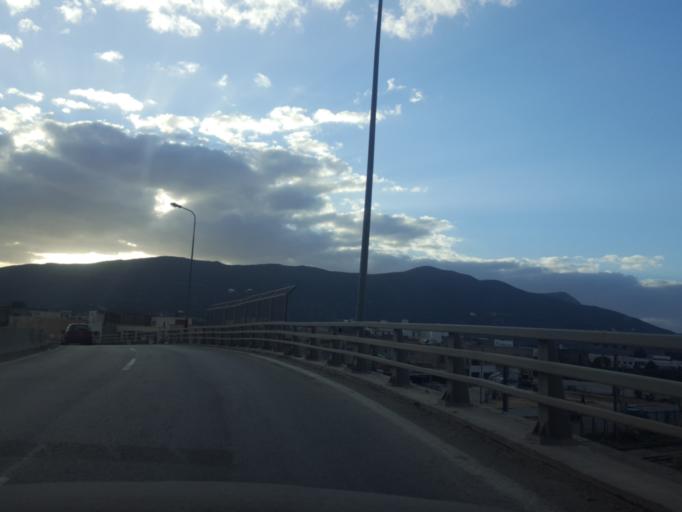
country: TN
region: Tunis
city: Hammam-Lif
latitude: 36.7011
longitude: 10.4036
